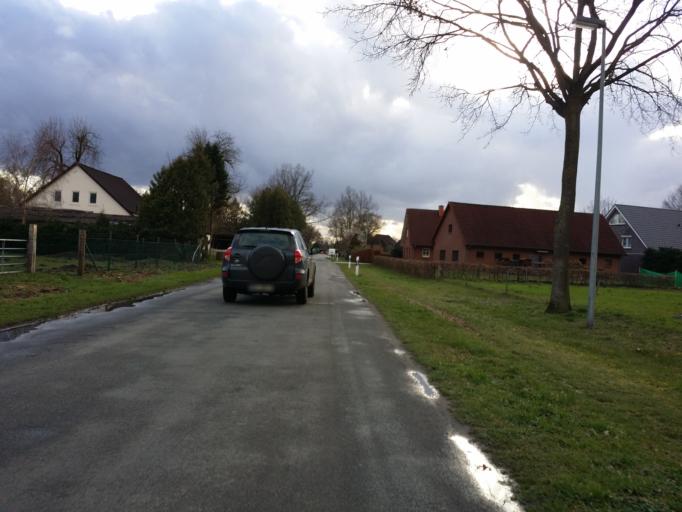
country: DE
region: Lower Saxony
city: Delmenhorst
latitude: 53.0227
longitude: 8.6337
